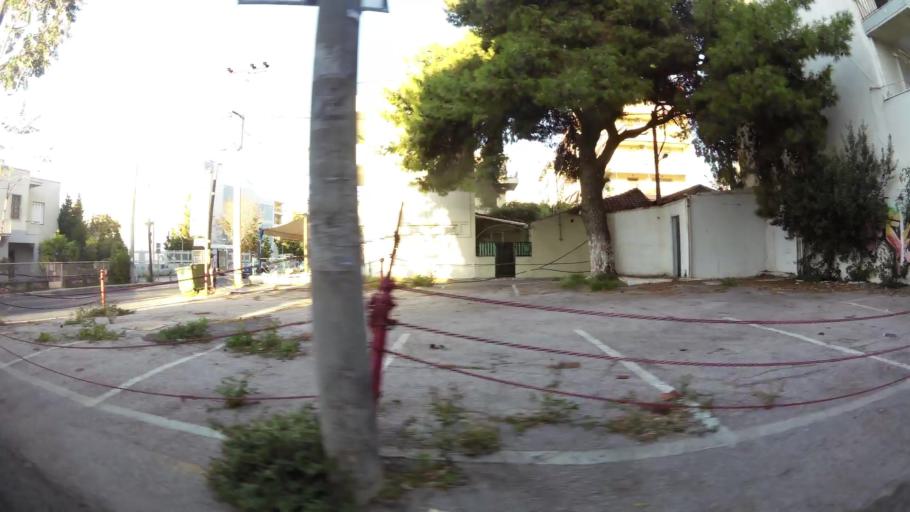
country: GR
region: Attica
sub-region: Nomarchia Athinas
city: Marousi
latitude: 38.0492
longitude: 23.8010
